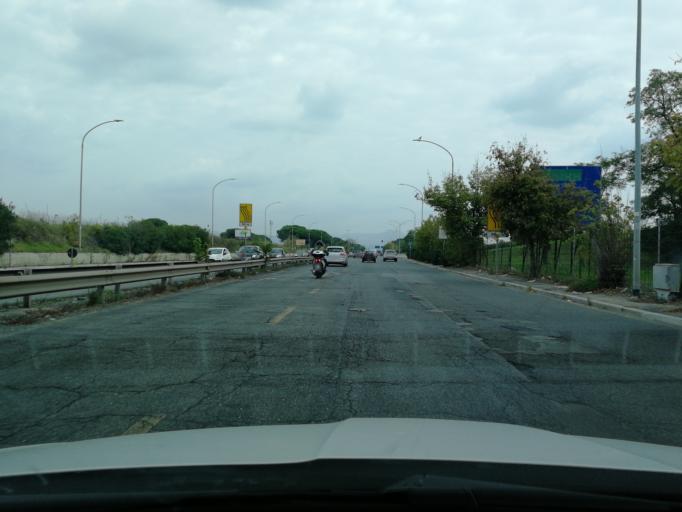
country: IT
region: Latium
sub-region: Citta metropolitana di Roma Capitale
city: Ciampino
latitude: 41.8476
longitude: 12.5769
